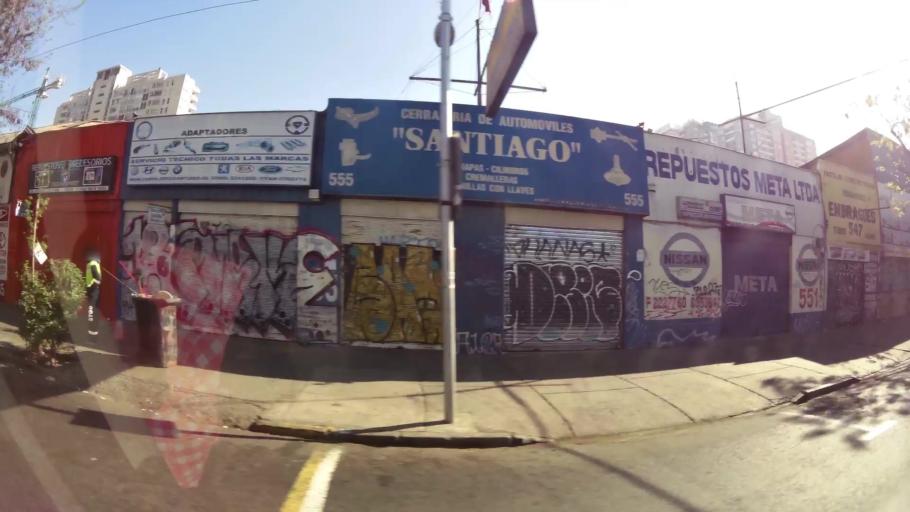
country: CL
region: Santiago Metropolitan
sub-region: Provincia de Santiago
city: Santiago
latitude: -33.4528
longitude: -70.6419
